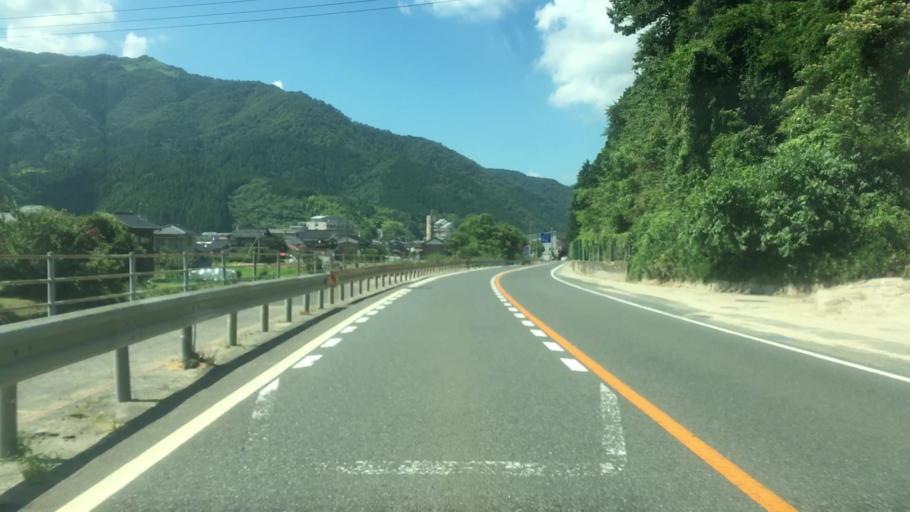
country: JP
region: Tottori
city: Tottori
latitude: 35.2577
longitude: 134.2282
